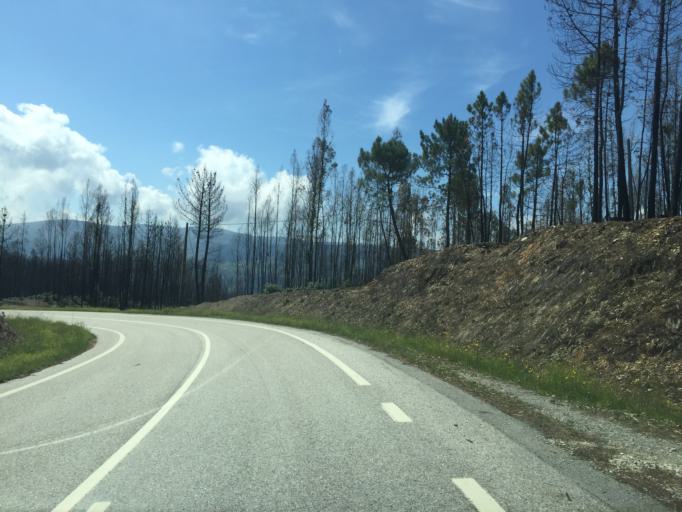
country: PT
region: Coimbra
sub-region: Pampilhosa da Serra
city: Pampilhosa da Serra
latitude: 39.9990
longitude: -7.9748
